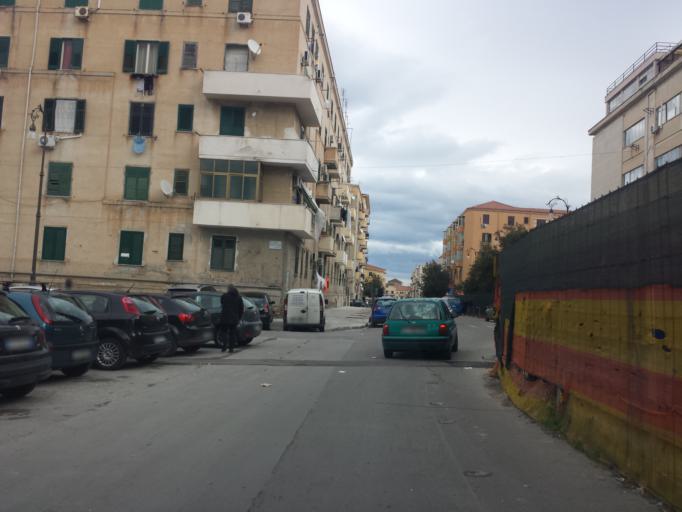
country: IT
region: Sicily
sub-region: Palermo
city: Palermo
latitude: 38.1096
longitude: 13.3553
